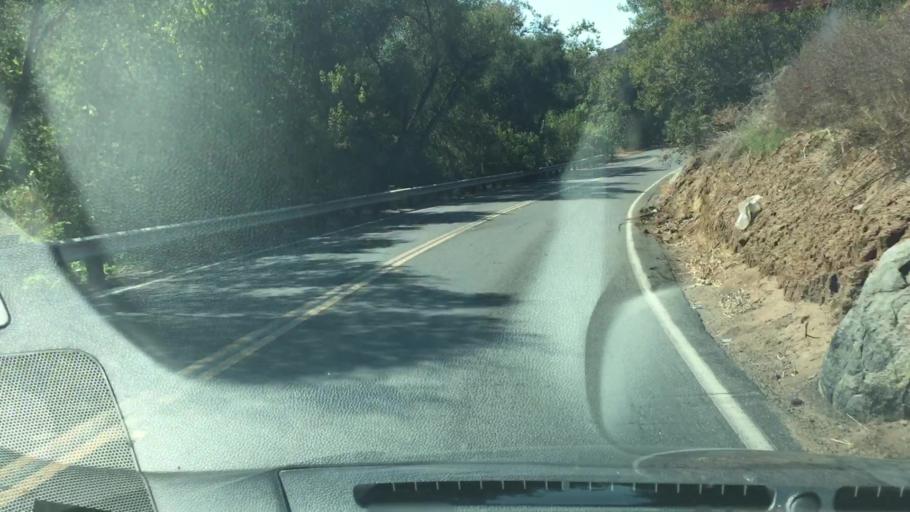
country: US
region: California
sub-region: San Diego County
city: Jamul
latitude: 32.7330
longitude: -116.8820
